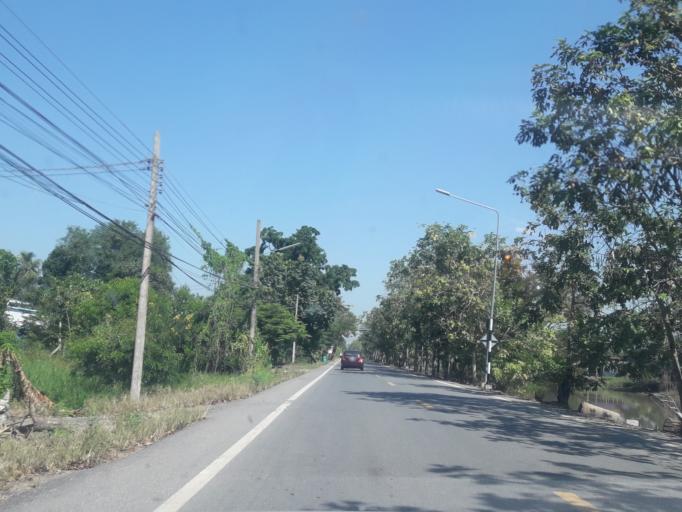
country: TH
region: Pathum Thani
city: Nong Suea
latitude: 14.1804
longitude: 100.8458
